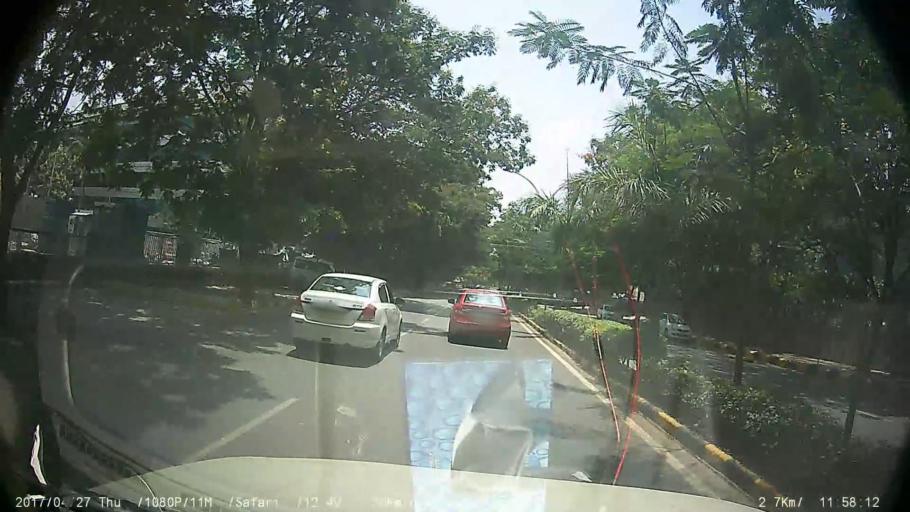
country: IN
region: Karnataka
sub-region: Bangalore Urban
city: Bangalore
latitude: 12.8541
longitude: 77.6613
